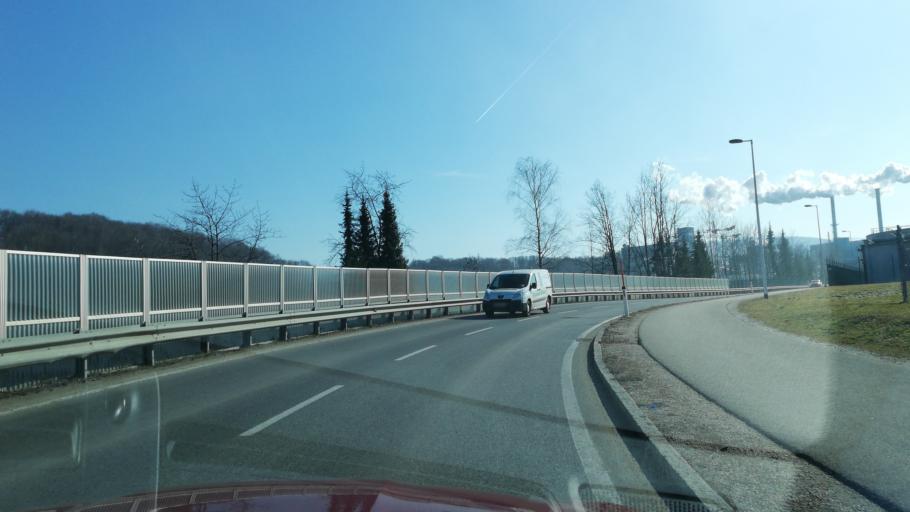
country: AT
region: Upper Austria
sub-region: Politischer Bezirk Vocklabruck
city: Lenzing
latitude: 47.9810
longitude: 13.6197
